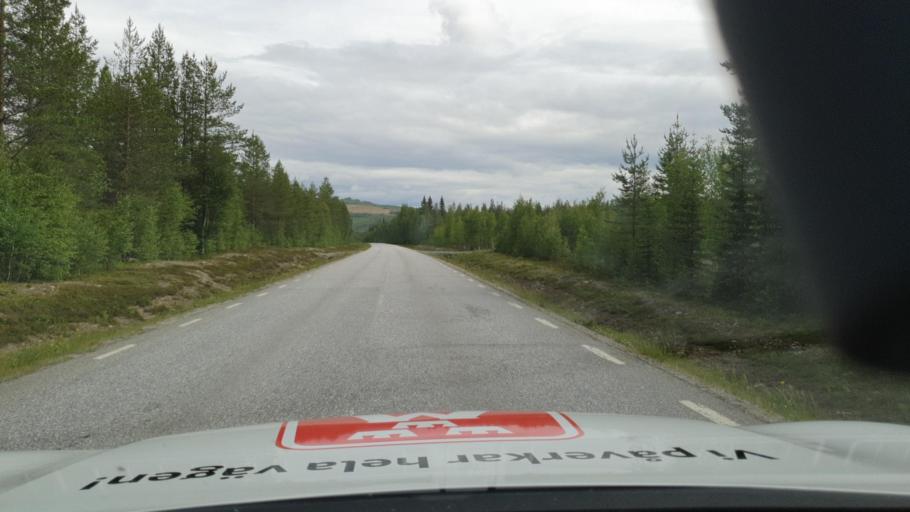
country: SE
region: Vaesterbotten
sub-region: Asele Kommun
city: Asele
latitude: 64.2134
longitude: 16.9132
